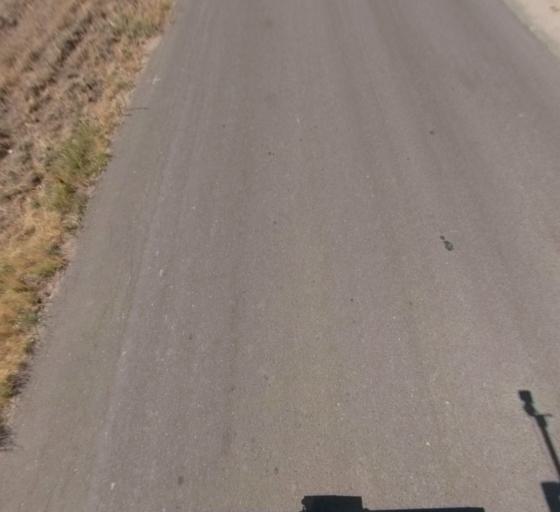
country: US
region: California
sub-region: Fresno County
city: Biola
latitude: 36.8663
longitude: -119.9471
